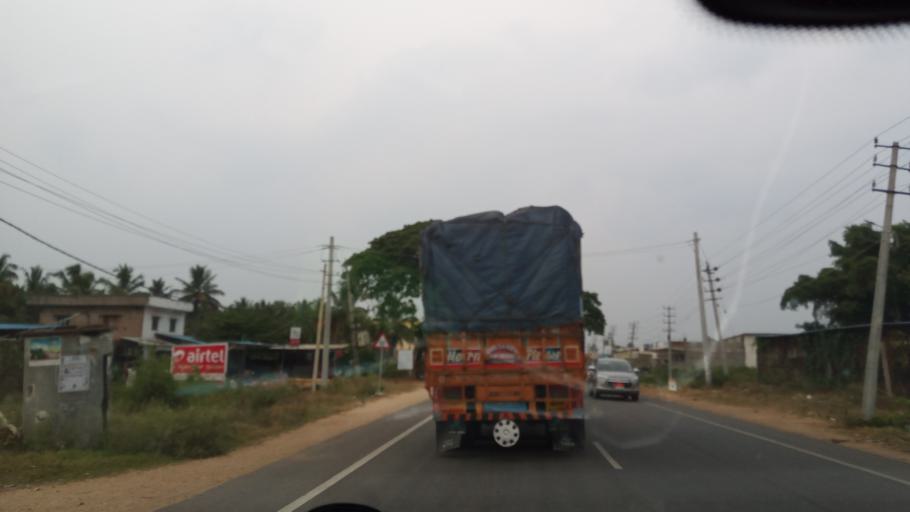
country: IN
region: Karnataka
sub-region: Mandya
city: Nagamangala
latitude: 12.8145
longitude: 76.7561
